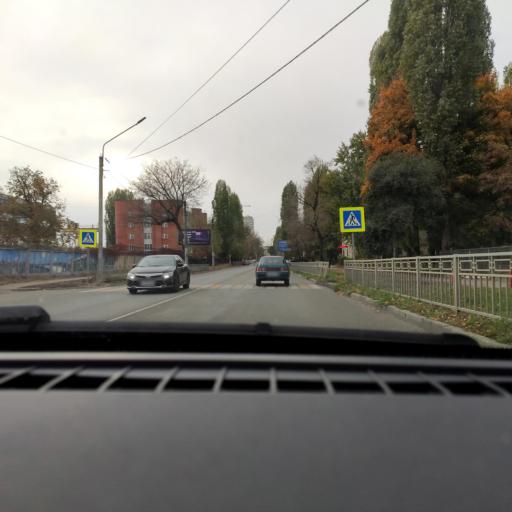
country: RU
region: Voronezj
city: Voronezh
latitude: 51.6808
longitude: 39.1955
